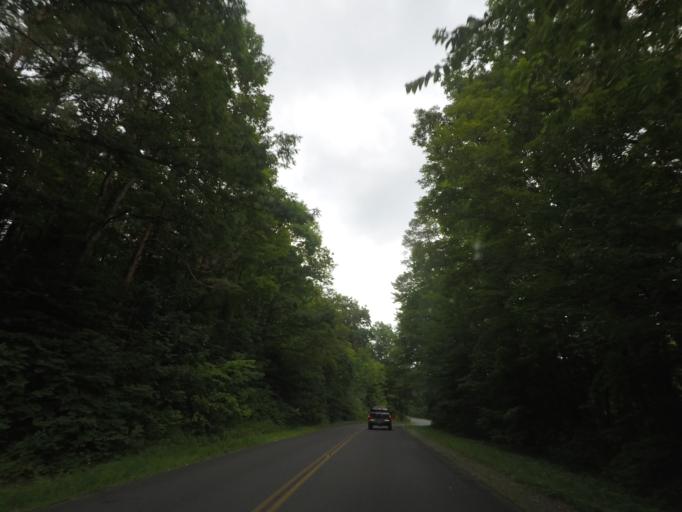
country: US
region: New York
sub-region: Rensselaer County
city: Poestenkill
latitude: 42.8392
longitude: -73.5266
